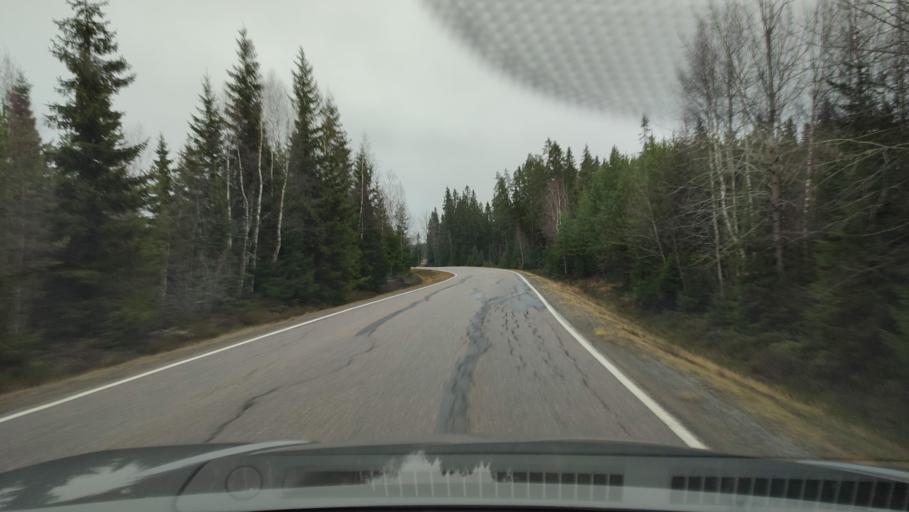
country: FI
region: Southern Ostrobothnia
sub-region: Suupohja
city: Isojoki
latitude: 62.2131
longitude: 21.9838
